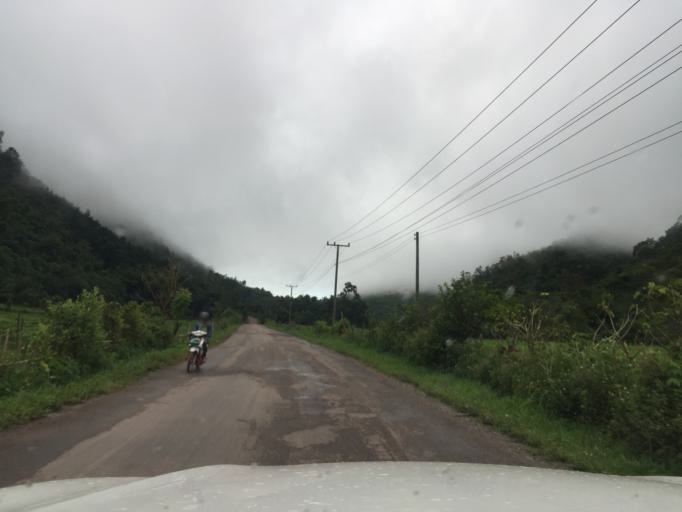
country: LA
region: Oudomxai
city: Muang La
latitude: 20.8325
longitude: 102.0992
